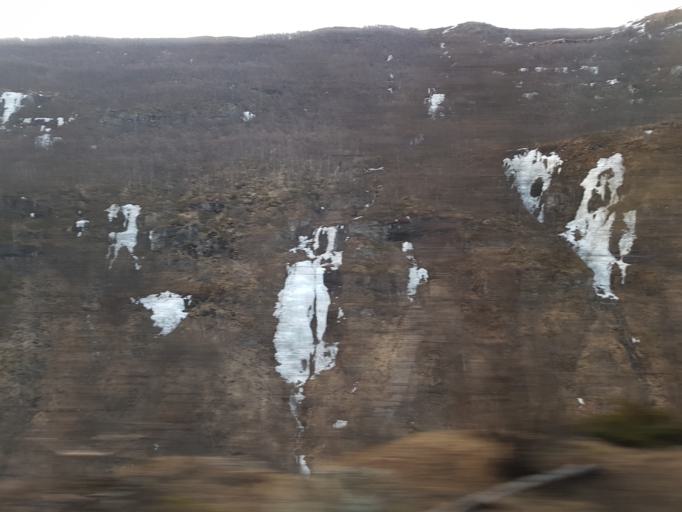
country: NO
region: Sor-Trondelag
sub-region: Oppdal
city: Oppdal
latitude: 62.3510
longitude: 9.6300
